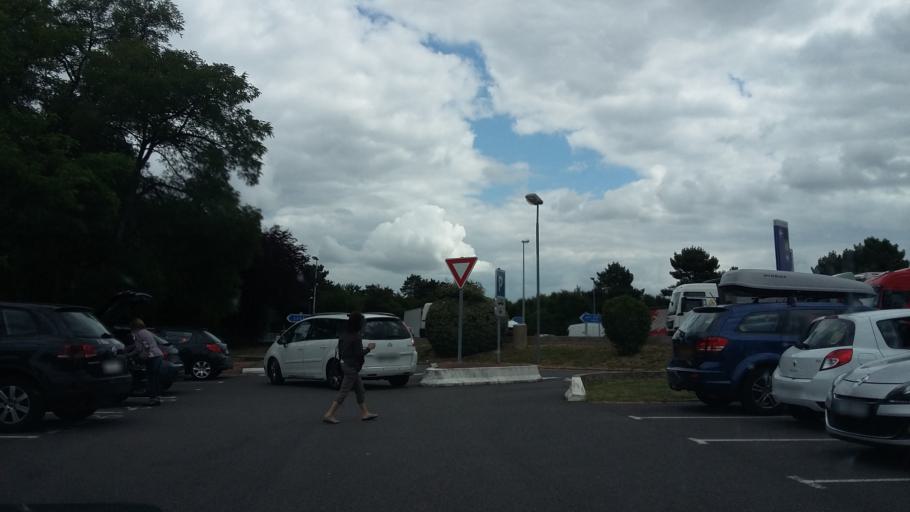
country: FR
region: Poitou-Charentes
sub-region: Departement de la Vienne
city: Antran
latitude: 46.9062
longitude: 0.5236
